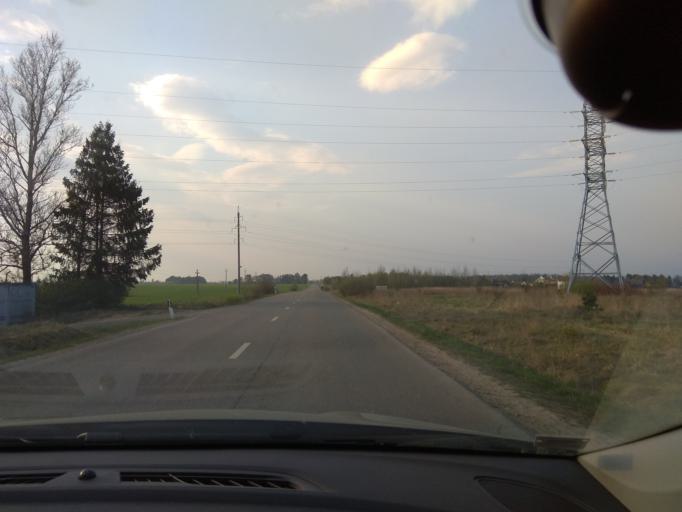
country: LT
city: Lentvaris
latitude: 54.6137
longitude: 25.1196
